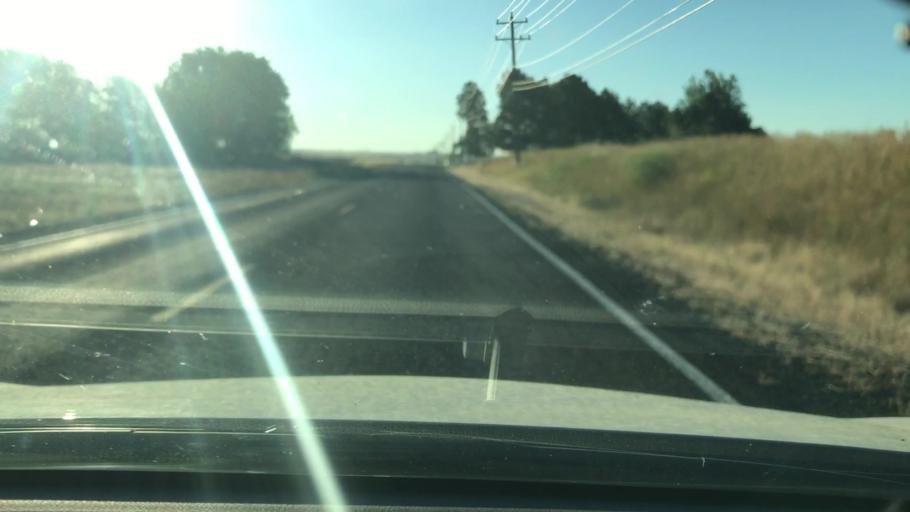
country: US
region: Washington
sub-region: Grant County
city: Moses Lake
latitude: 47.1163
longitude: -119.2428
